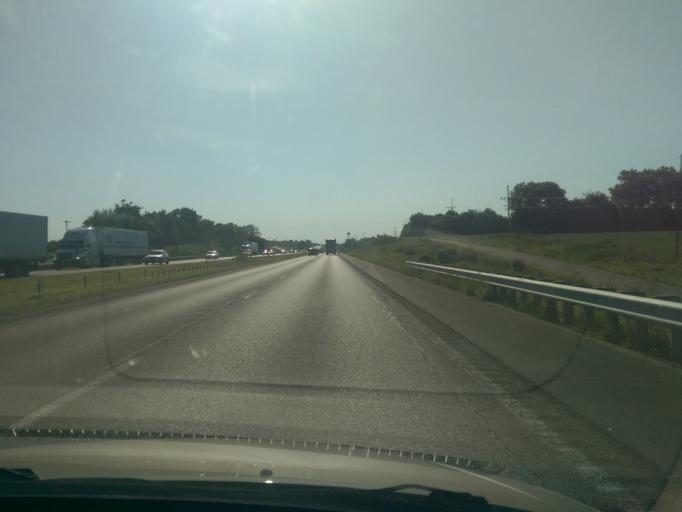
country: US
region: Missouri
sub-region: Lafayette County
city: Higginsville
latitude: 39.0024
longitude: -93.8005
